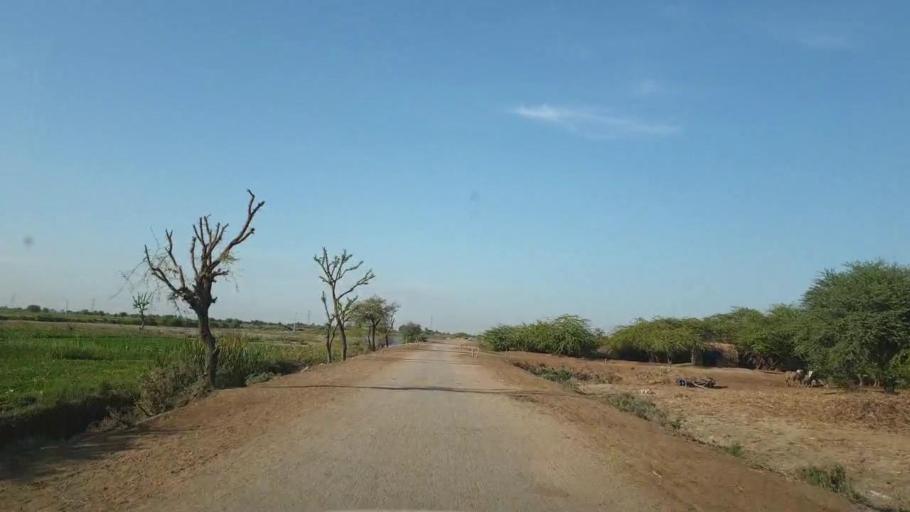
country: PK
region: Sindh
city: Kunri
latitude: 25.0946
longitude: 69.4204
